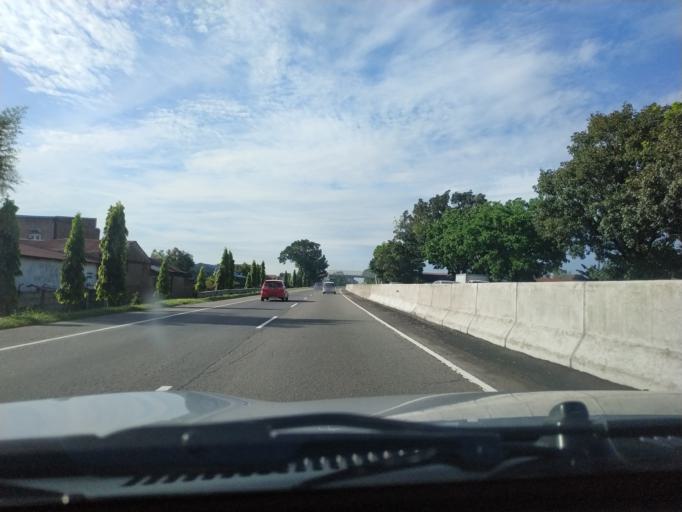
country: ID
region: North Sumatra
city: Medan
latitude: 3.5681
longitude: 98.7259
